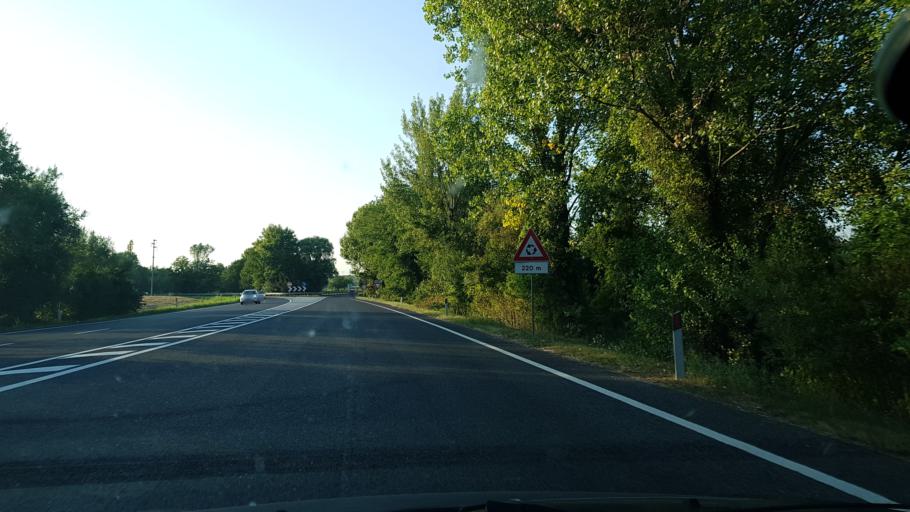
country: IT
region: Friuli Venezia Giulia
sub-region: Provincia di Gorizia
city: Ronchi dei Legionari
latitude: 45.8345
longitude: 13.4914
